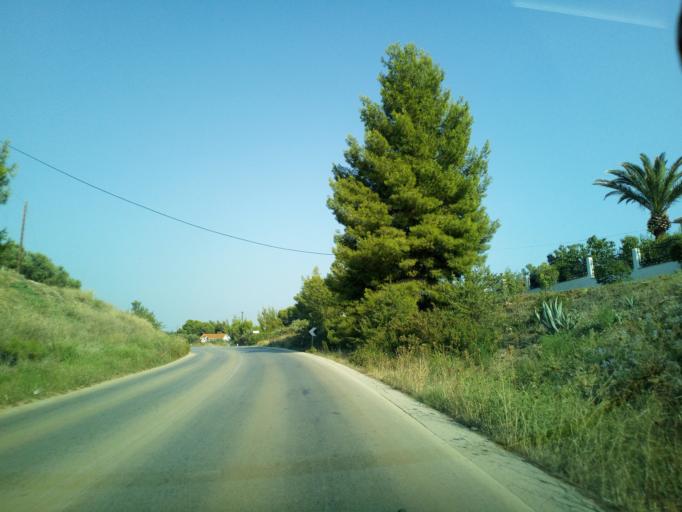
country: GR
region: Central Macedonia
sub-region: Nomos Chalkidikis
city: Nikiti
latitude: 40.2310
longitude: 23.6190
